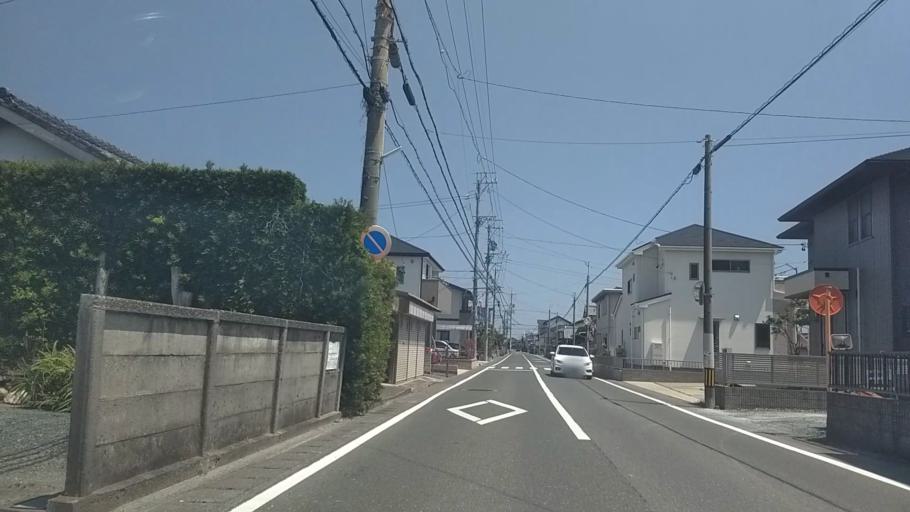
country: JP
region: Shizuoka
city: Hamamatsu
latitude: 34.6831
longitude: 137.6377
